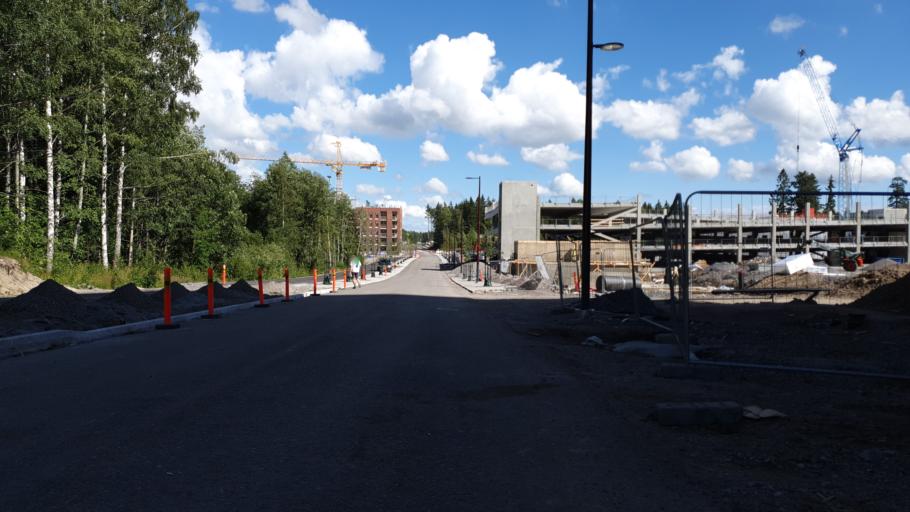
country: FI
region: Uusimaa
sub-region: Helsinki
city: Tuusula
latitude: 60.3998
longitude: 25.0344
